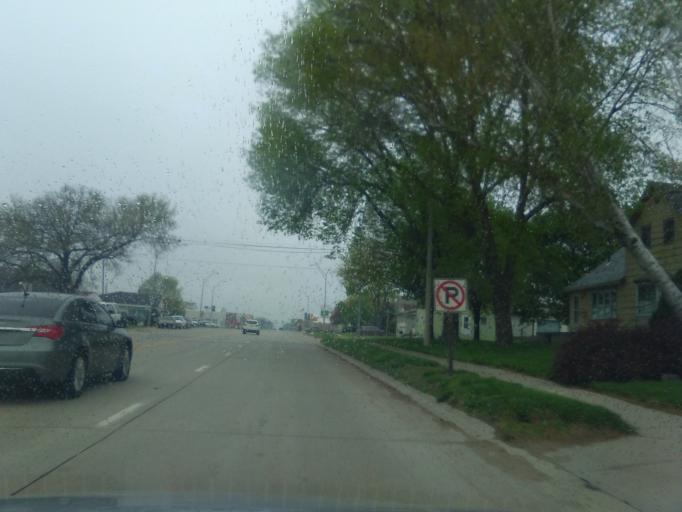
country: US
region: Nebraska
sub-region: Cuming County
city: Wisner
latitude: 41.9852
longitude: -96.9103
